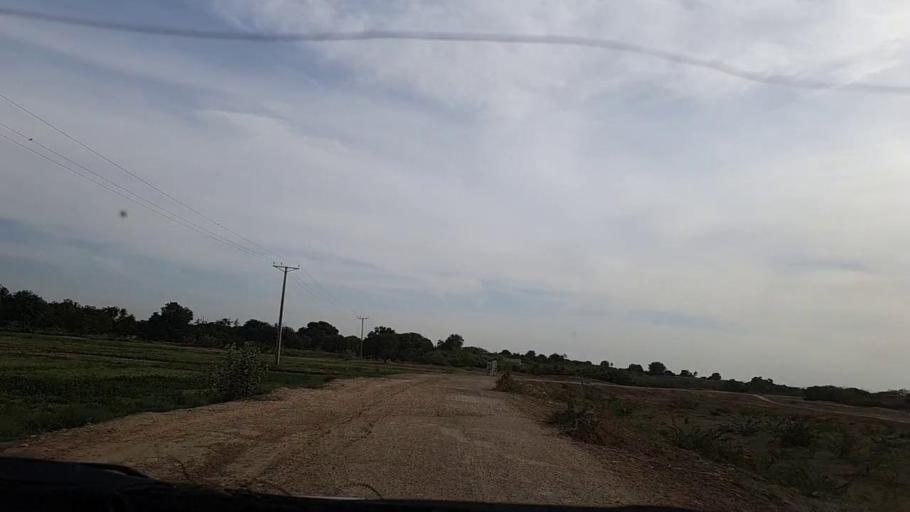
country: PK
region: Sindh
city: Dhoro Naro
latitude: 25.4158
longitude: 69.5211
